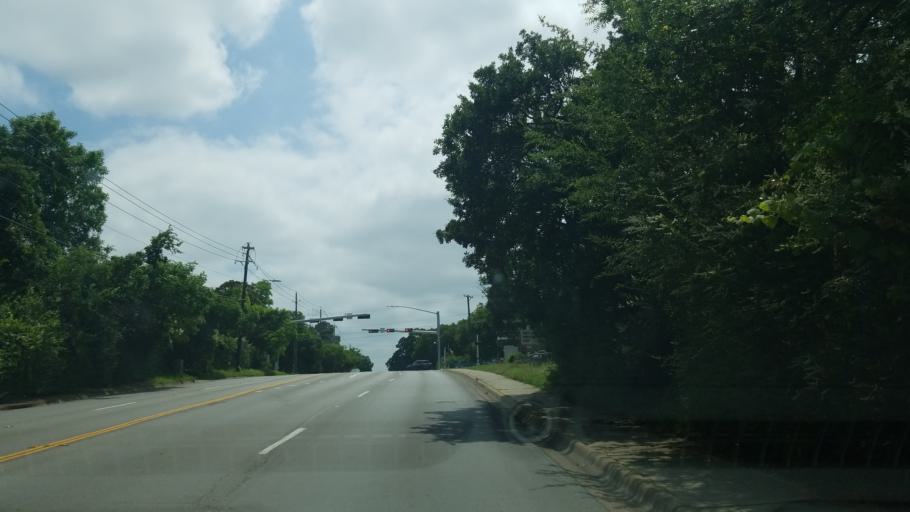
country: US
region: Texas
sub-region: Denton County
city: Denton
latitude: 33.2347
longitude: -97.1262
